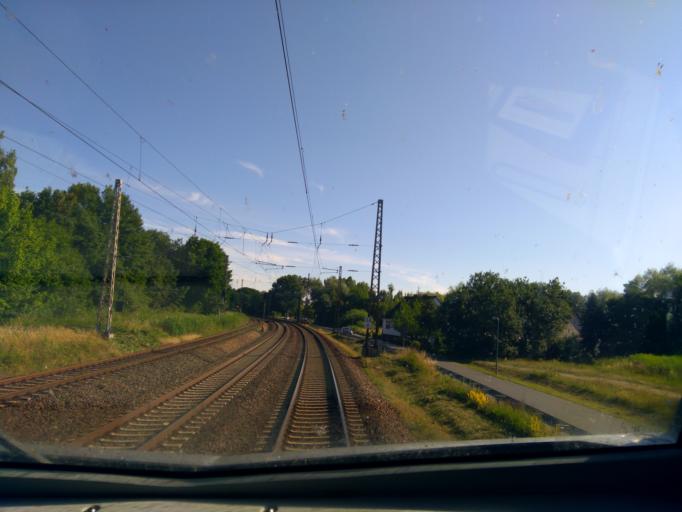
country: DE
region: Brandenburg
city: Bestensee
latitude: 52.2347
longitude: 13.6342
